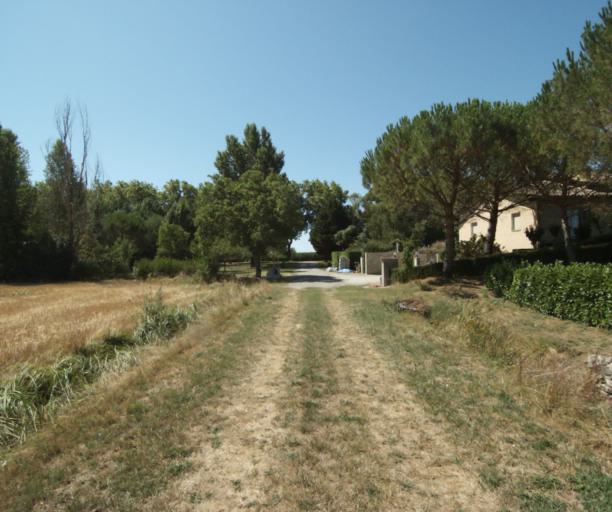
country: FR
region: Midi-Pyrenees
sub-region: Departement de la Haute-Garonne
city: Revel
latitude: 43.4992
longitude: 1.9607
